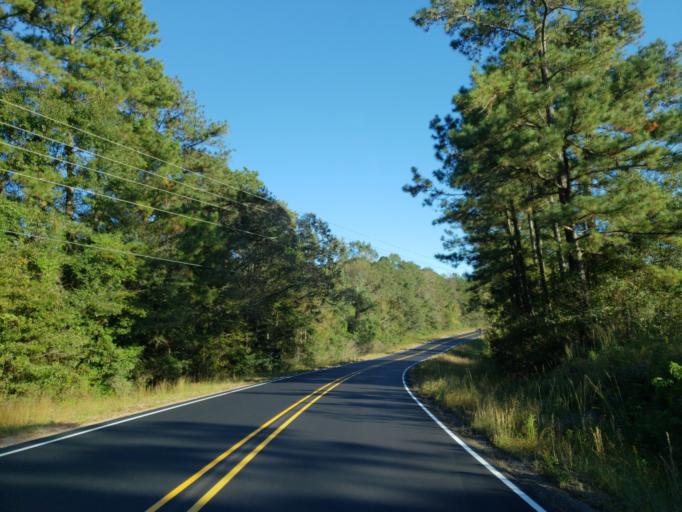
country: US
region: Mississippi
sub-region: Perry County
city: Richton
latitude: 31.3558
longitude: -88.7882
